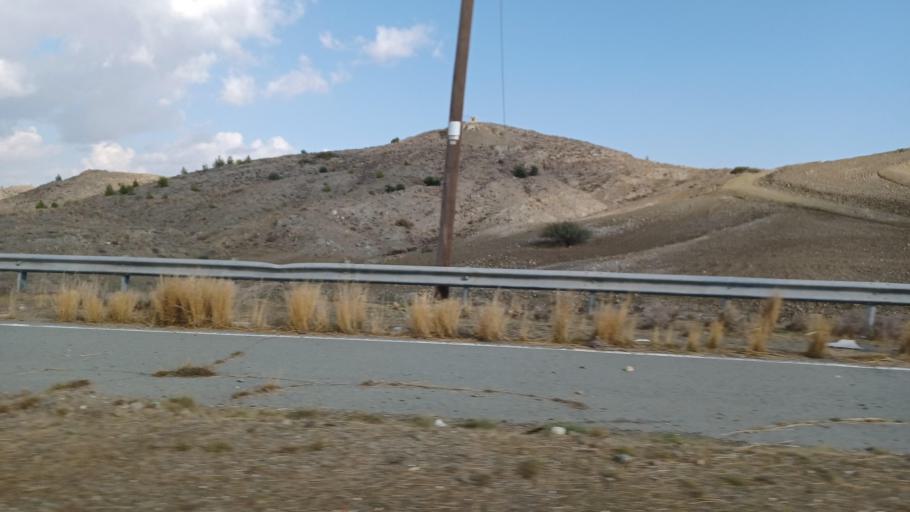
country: CY
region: Larnaka
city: Troulloi
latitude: 35.0088
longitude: 33.6248
